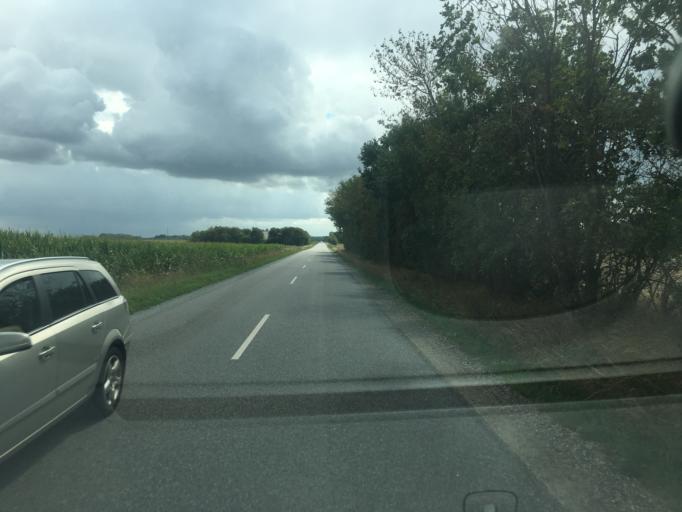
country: DK
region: South Denmark
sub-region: Tonder Kommune
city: Logumkloster
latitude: 55.0466
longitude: 8.9611
